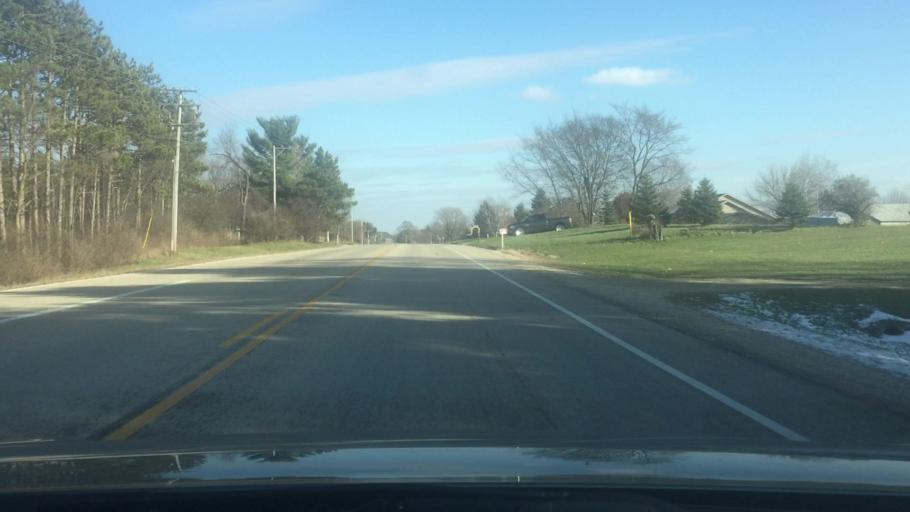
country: US
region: Wisconsin
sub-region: Jefferson County
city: Fort Atkinson
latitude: 42.9392
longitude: -88.7786
